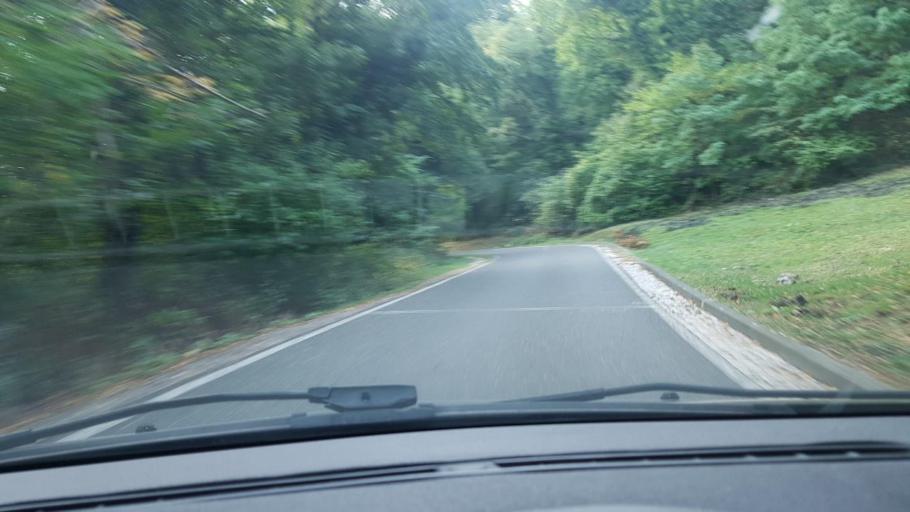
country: HR
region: Grad Zagreb
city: Zagreb
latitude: 45.8624
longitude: 15.9470
